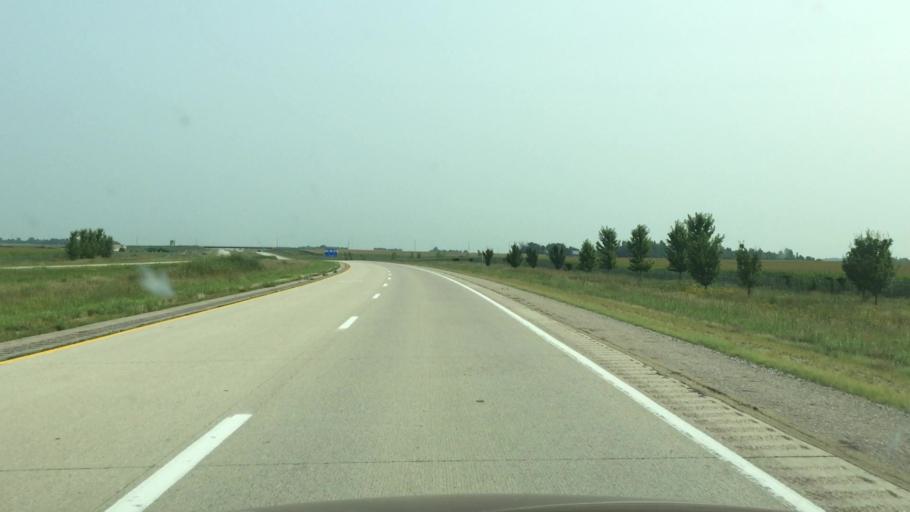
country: US
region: Iowa
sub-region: Osceola County
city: Sibley
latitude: 43.3935
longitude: -95.7179
